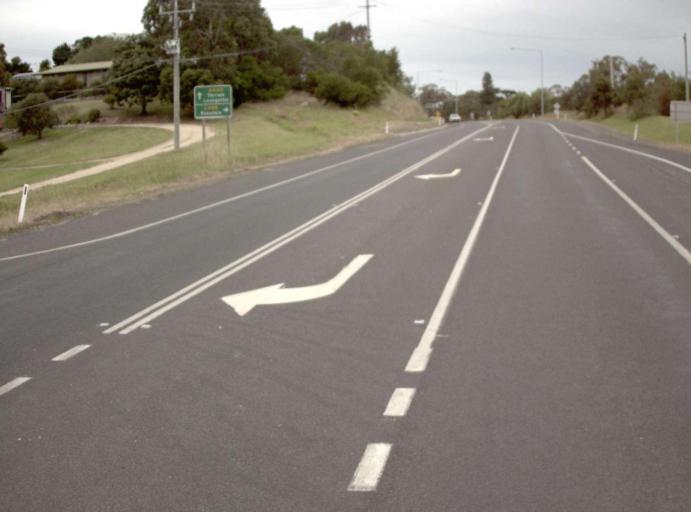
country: AU
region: Victoria
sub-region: Wellington
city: Sale
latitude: -38.1567
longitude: 147.0838
